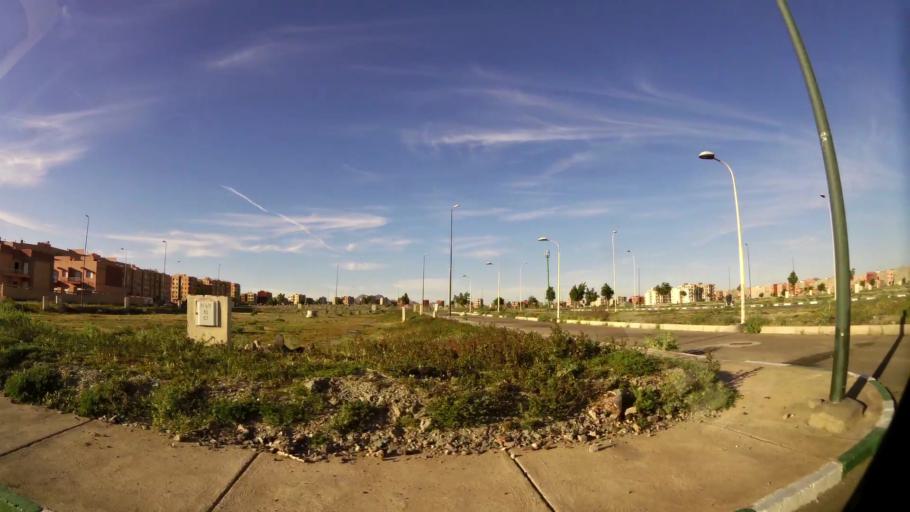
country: MA
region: Marrakech-Tensift-Al Haouz
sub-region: Marrakech
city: Marrakesh
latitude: 31.7618
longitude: -8.1079
